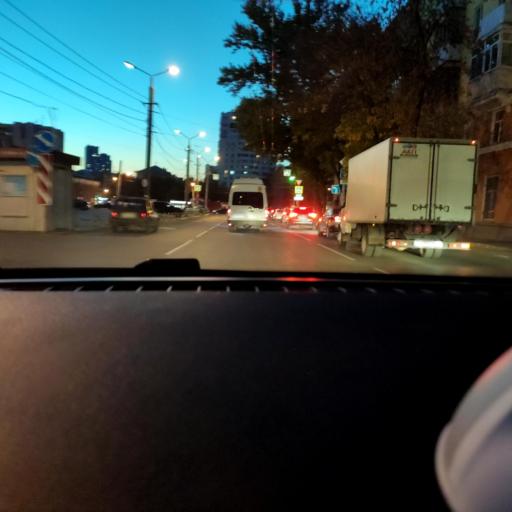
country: RU
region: Samara
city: Samara
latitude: 53.1952
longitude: 50.1266
